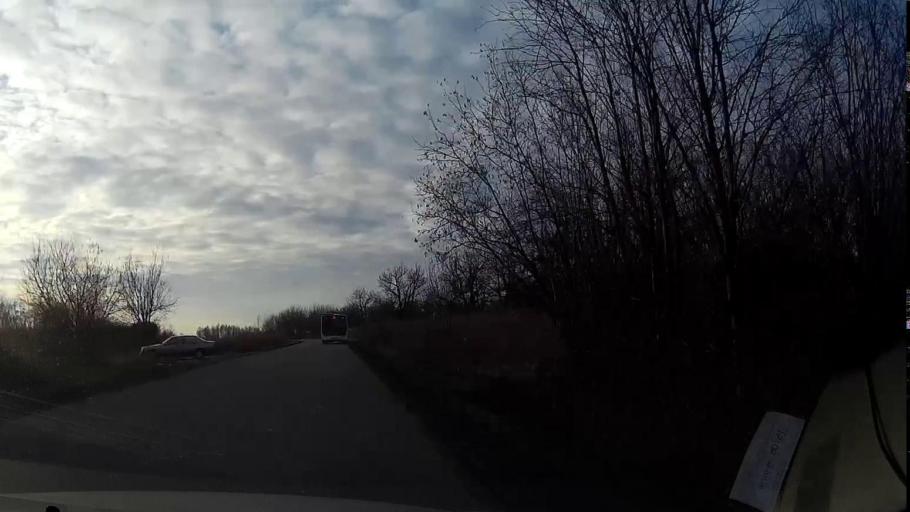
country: PL
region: Lesser Poland Voivodeship
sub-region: Powiat krakowski
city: Czulow
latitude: 50.0642
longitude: 19.6792
